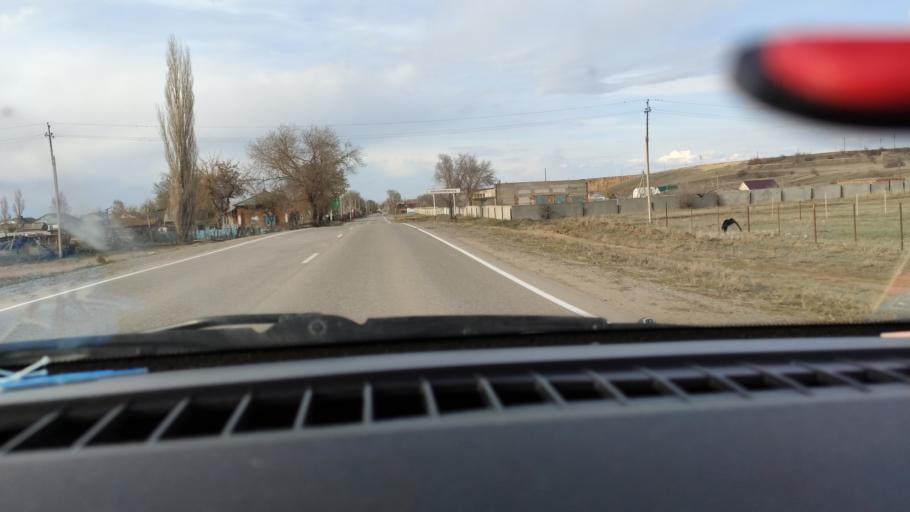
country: RU
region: Saratov
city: Privolzhskiy
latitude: 51.2022
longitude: 45.9168
